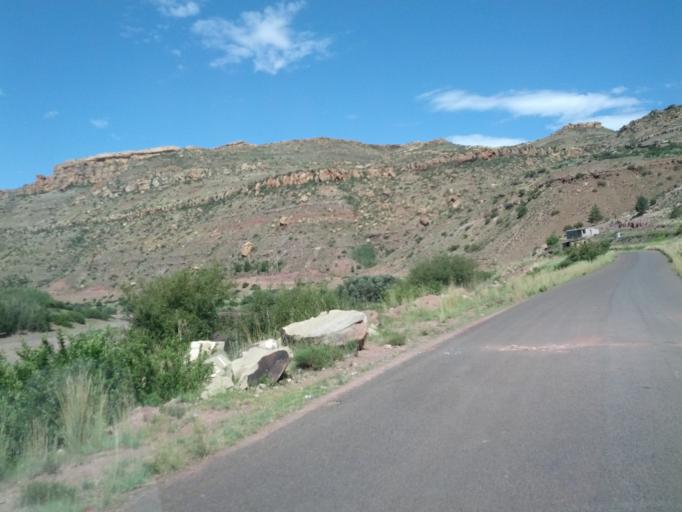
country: LS
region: Qacha's Nek
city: Qacha's Nek
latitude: -30.0736
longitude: 28.4460
